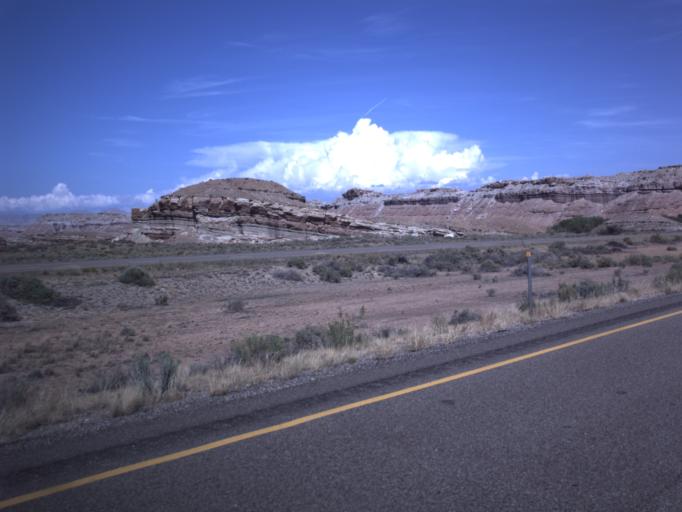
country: US
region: Utah
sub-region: Carbon County
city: East Carbon City
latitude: 38.9246
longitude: -110.4150
